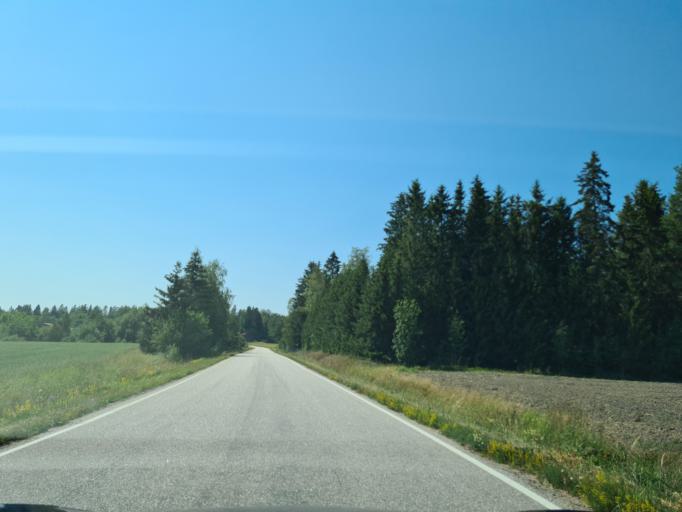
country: FI
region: Varsinais-Suomi
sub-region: Turku
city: Tarvasjoki
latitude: 60.5979
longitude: 22.6750
